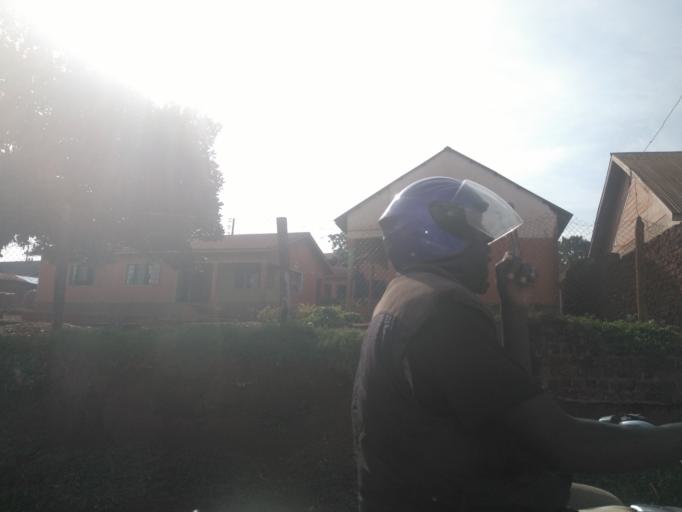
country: UG
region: Central Region
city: Kampala Central Division
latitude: 0.3611
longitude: 32.5699
